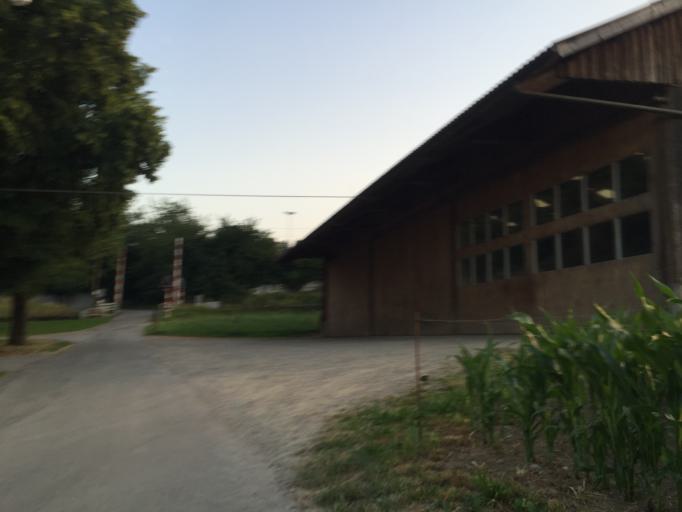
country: CH
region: Bern
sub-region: Bern-Mittelland District
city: Bern
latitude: 46.9316
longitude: 7.4382
